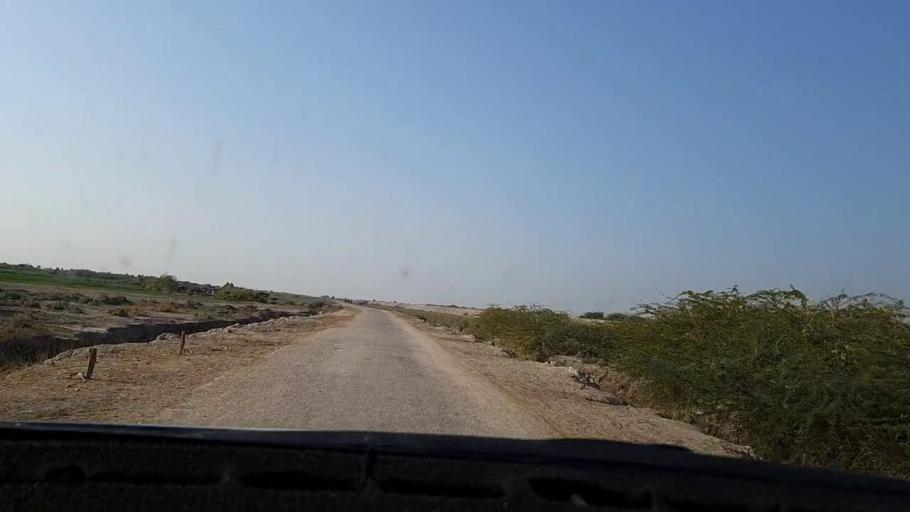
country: PK
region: Sindh
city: Tando Mittha Khan
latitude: 25.8321
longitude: 69.3182
